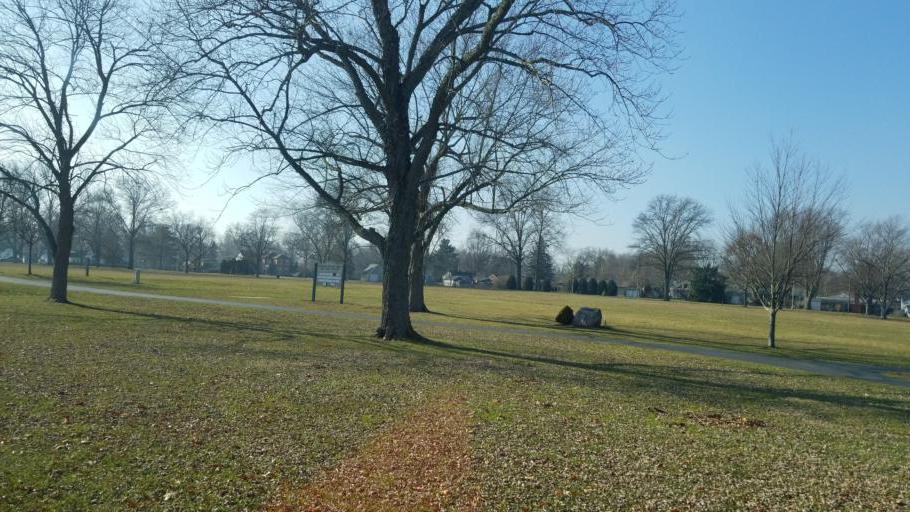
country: US
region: Ohio
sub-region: Seneca County
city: Tiffin
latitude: 41.1042
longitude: -83.1578
